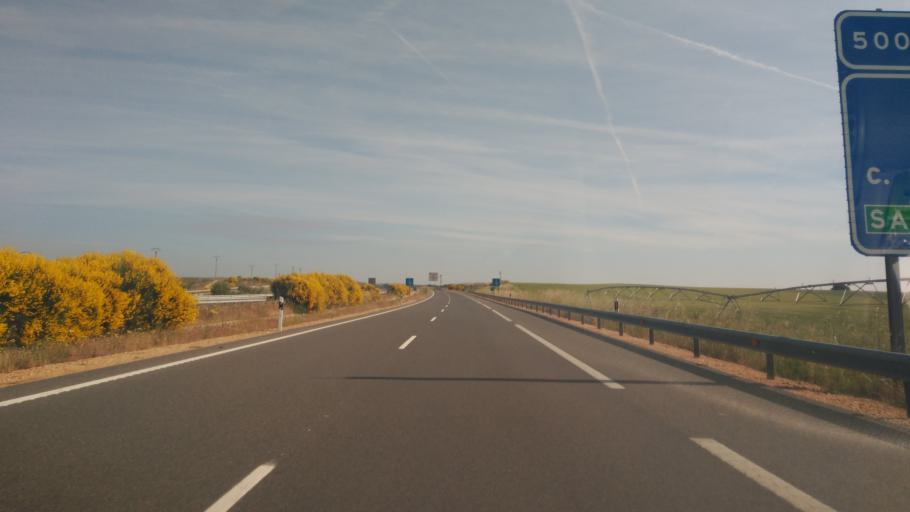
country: ES
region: Castille and Leon
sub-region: Provincia de Salamanca
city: Calzada de Valdunciel
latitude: 41.1128
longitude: -5.6986
